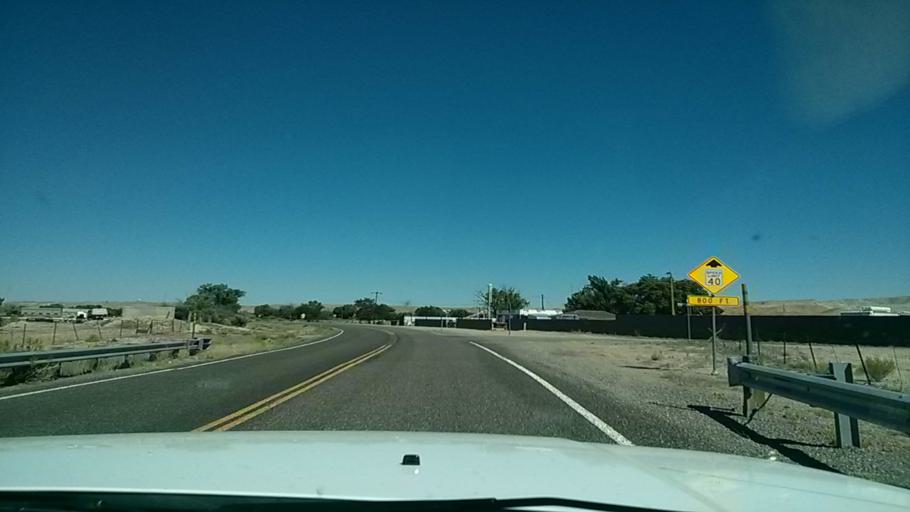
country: US
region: Utah
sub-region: Emery County
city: Ferron
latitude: 38.3751
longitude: -110.7296
